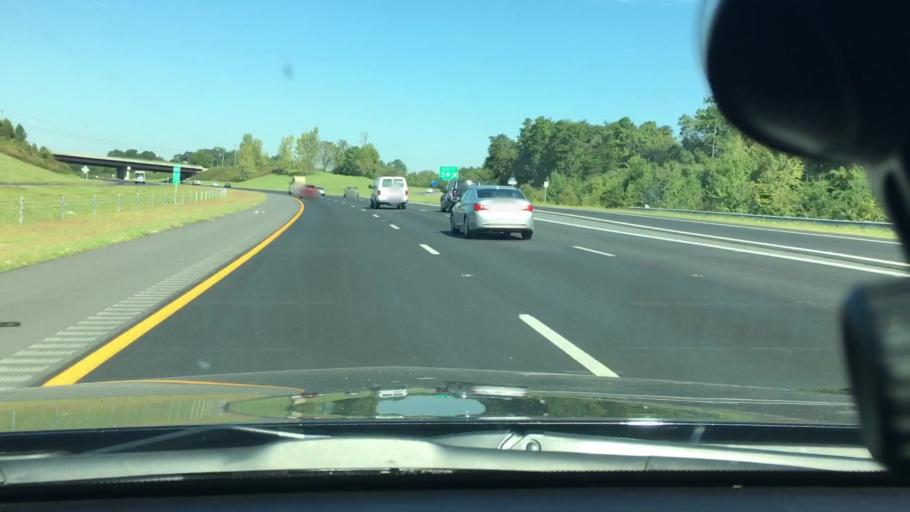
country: US
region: North Carolina
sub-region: Mecklenburg County
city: Mint Hill
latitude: 35.2501
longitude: -80.6512
